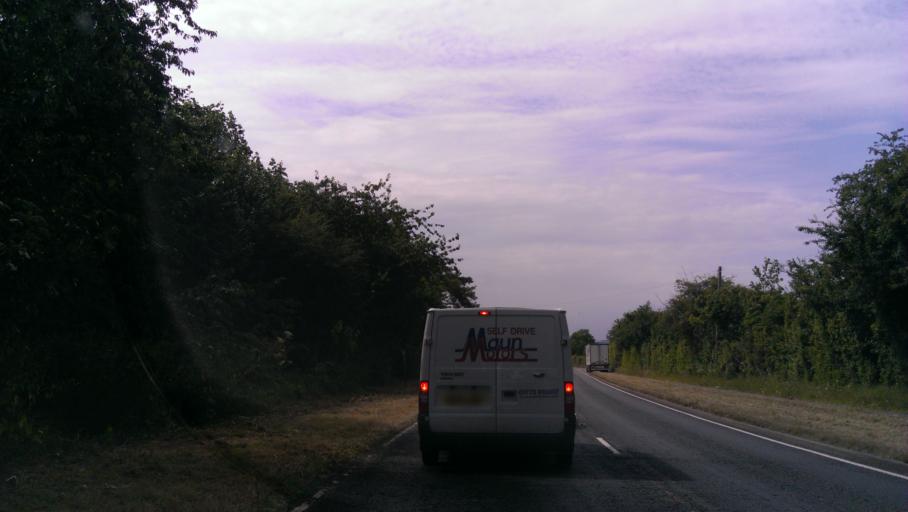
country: GB
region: England
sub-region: Kent
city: Teynham
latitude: 51.3199
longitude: 0.8306
